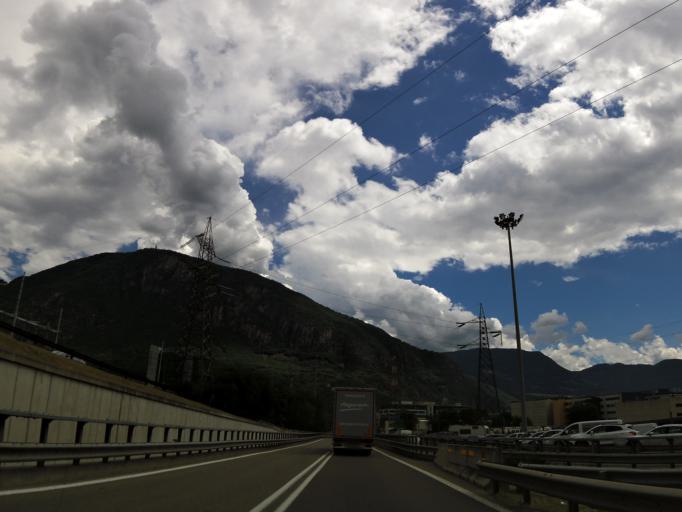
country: IT
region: Trentino-Alto Adige
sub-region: Bolzano
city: Bolzano
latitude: 46.4770
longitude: 11.3197
